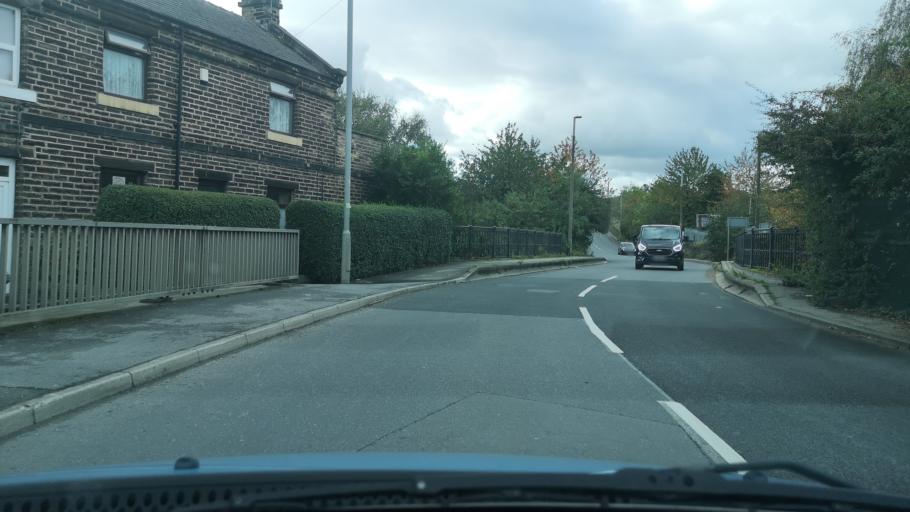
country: GB
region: England
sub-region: Kirklees
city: Dewsbury
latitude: 53.6787
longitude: -1.6215
